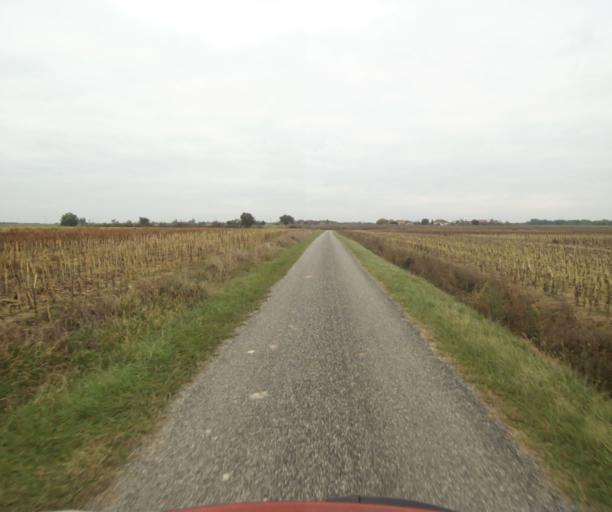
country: FR
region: Midi-Pyrenees
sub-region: Departement de la Haute-Garonne
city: Launac
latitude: 43.8027
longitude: 1.1926
